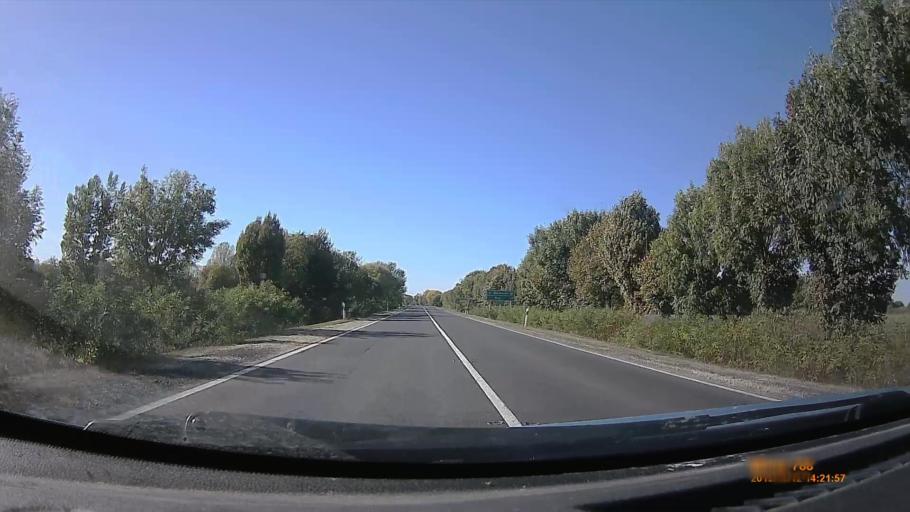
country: HU
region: Hajdu-Bihar
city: Biharkeresztes
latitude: 47.1411
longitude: 21.7240
